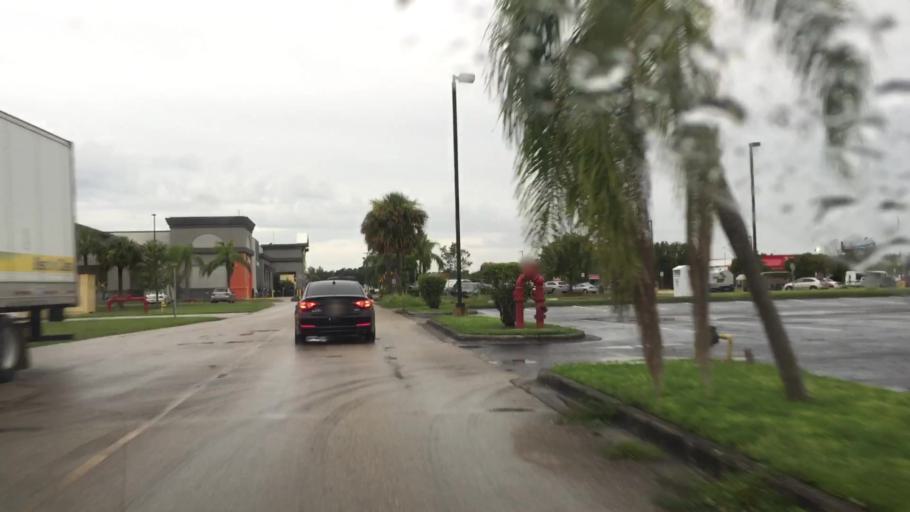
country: US
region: Florida
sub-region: Lee County
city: McGregor
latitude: 26.5554
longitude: -81.9048
